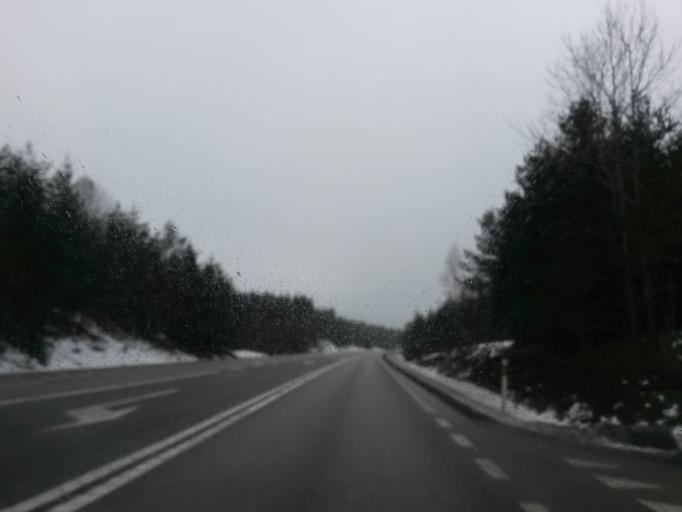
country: SE
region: Vaestra Goetaland
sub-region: Marks Kommun
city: Fritsla
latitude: 57.5219
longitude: 12.7748
